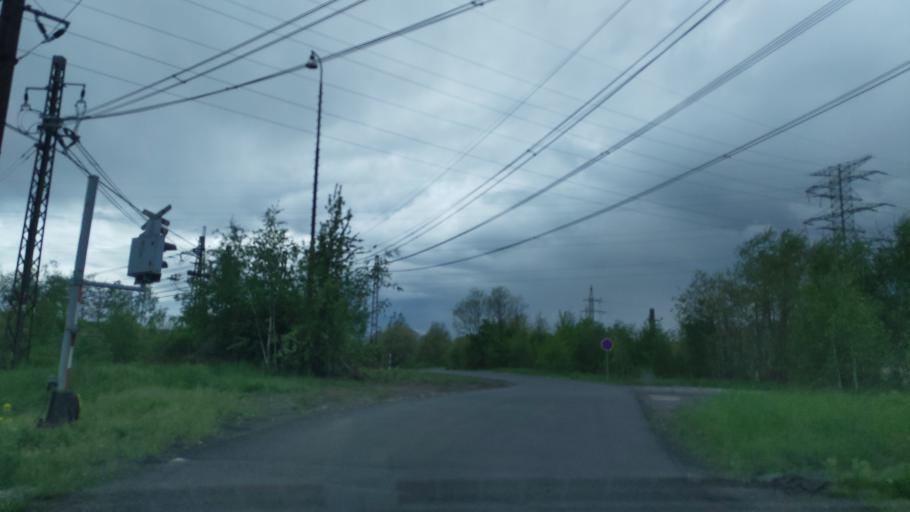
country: CZ
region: Ustecky
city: Trmice
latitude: 50.6461
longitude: 13.9811
